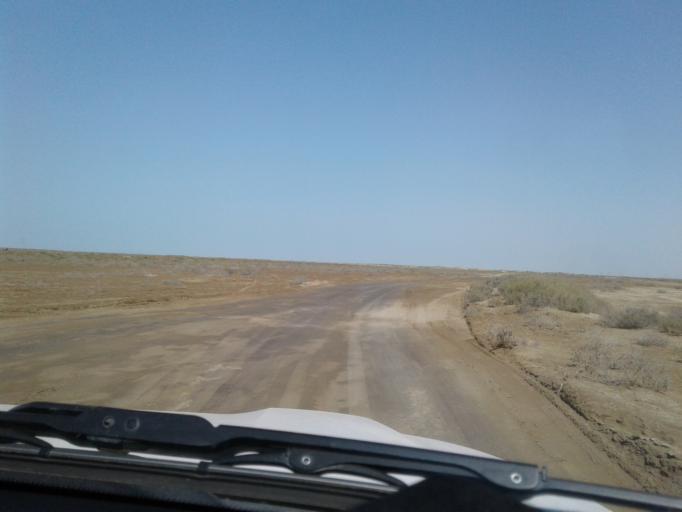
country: IR
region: Golestan
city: Gomishan
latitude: 37.8527
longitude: 53.8816
